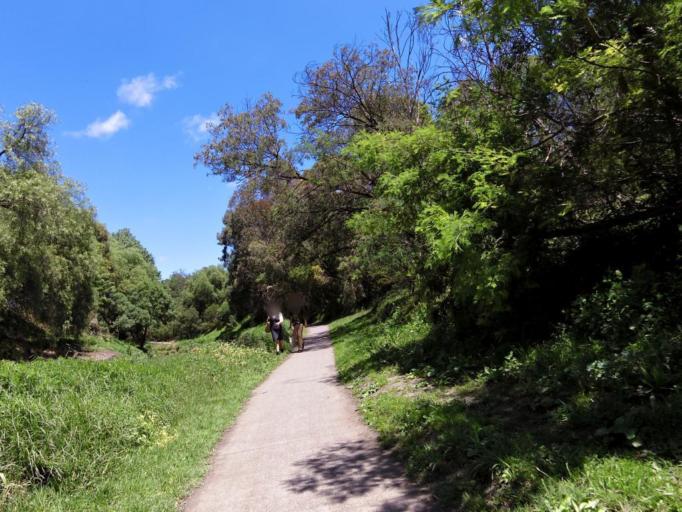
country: AU
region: Victoria
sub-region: Darebin
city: Northcote
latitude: -37.7756
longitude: 144.9885
